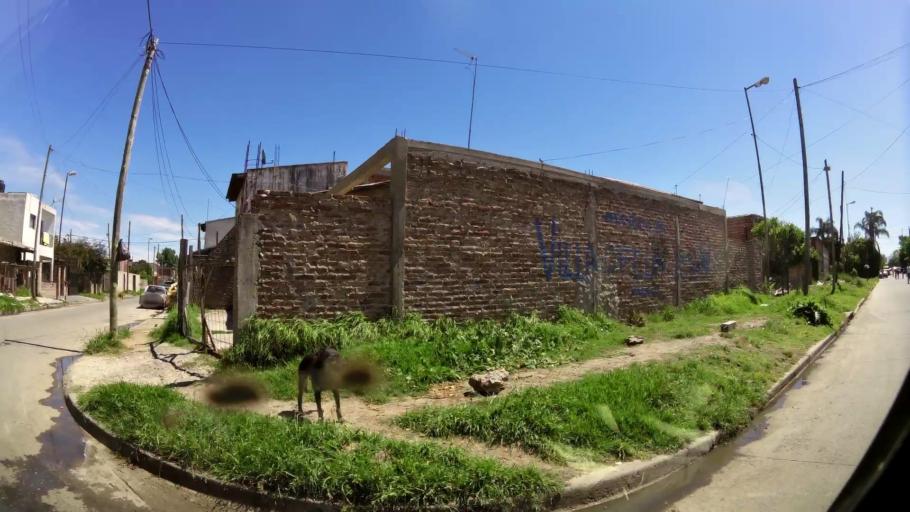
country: AR
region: Buenos Aires
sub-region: Partido de Lanus
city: Lanus
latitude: -34.7294
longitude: -58.3379
